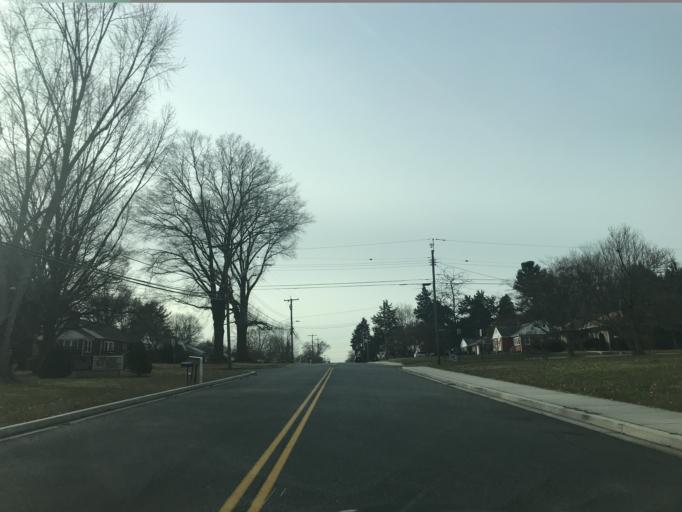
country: US
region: Maryland
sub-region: Harford County
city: Aberdeen
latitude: 39.5180
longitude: -76.1654
